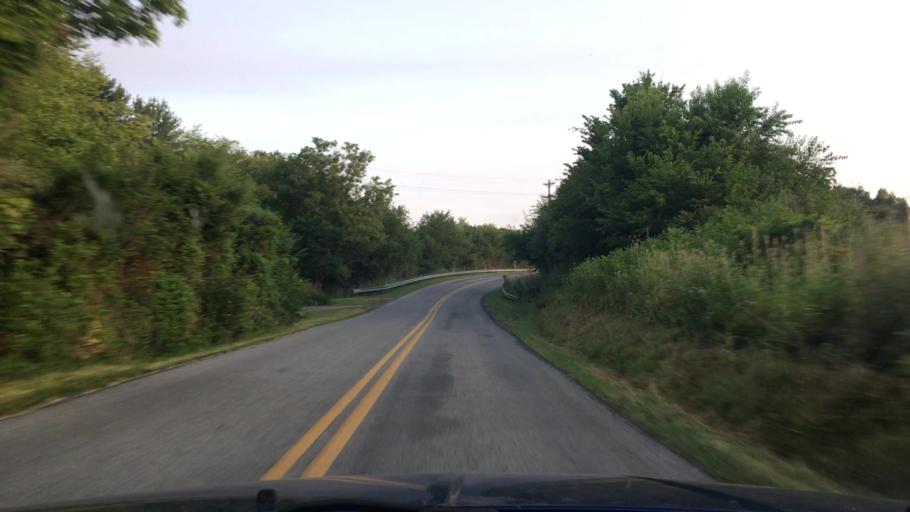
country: US
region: Virginia
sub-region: Augusta County
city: Verona
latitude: 38.2345
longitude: -78.9652
